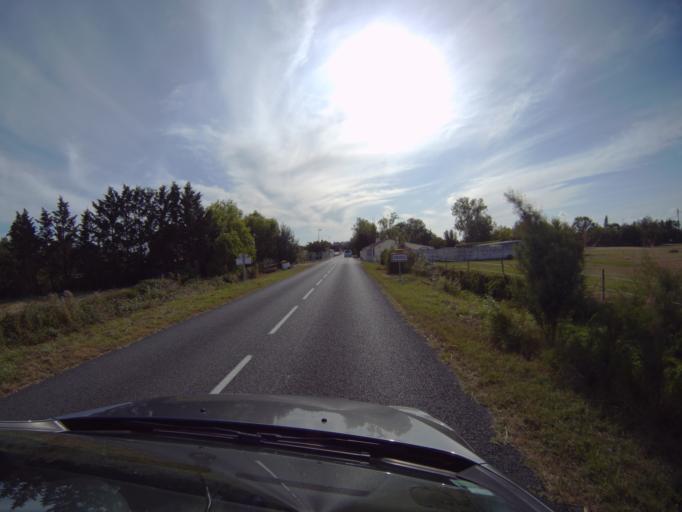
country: FR
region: Pays de la Loire
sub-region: Departement de la Vendee
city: Triaize
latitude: 46.4007
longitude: -1.2949
